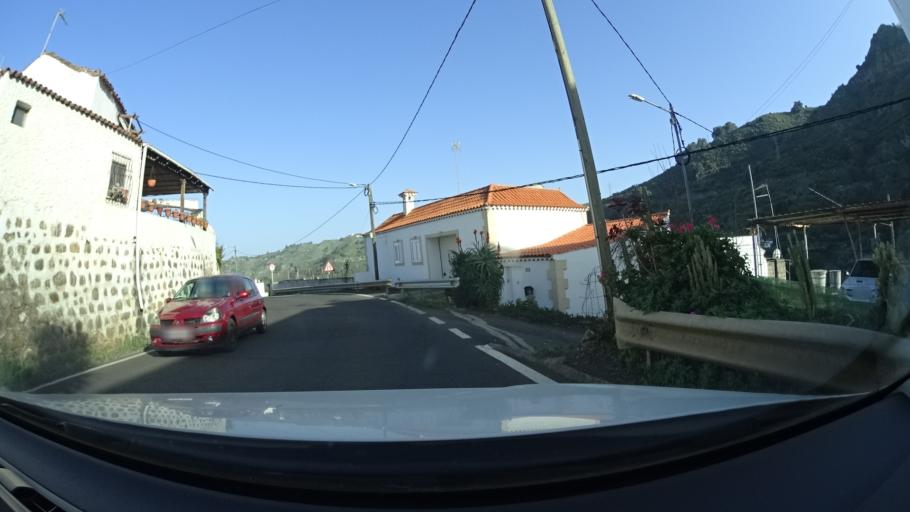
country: ES
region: Canary Islands
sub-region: Provincia de Las Palmas
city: Teror
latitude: 28.0579
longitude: -15.5540
